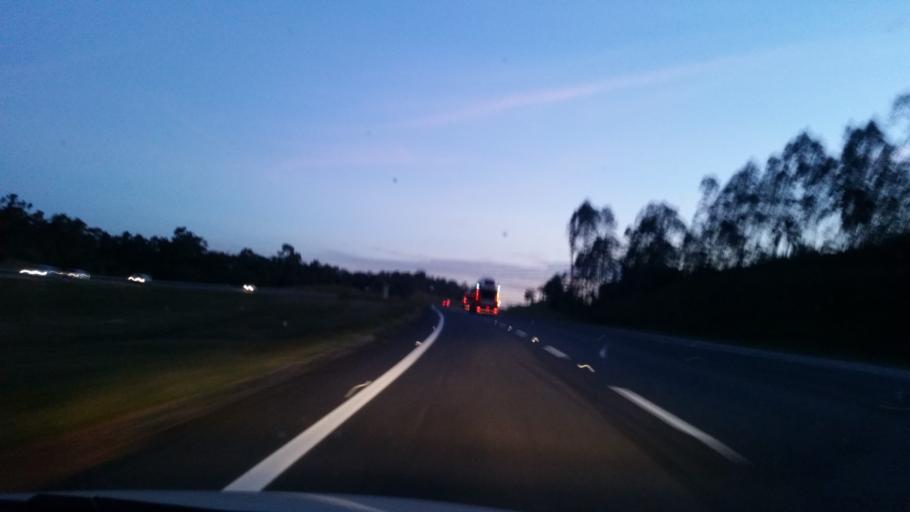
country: BR
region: Sao Paulo
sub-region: Santa Isabel
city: Santa Isabel
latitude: -23.3657
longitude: -46.1320
